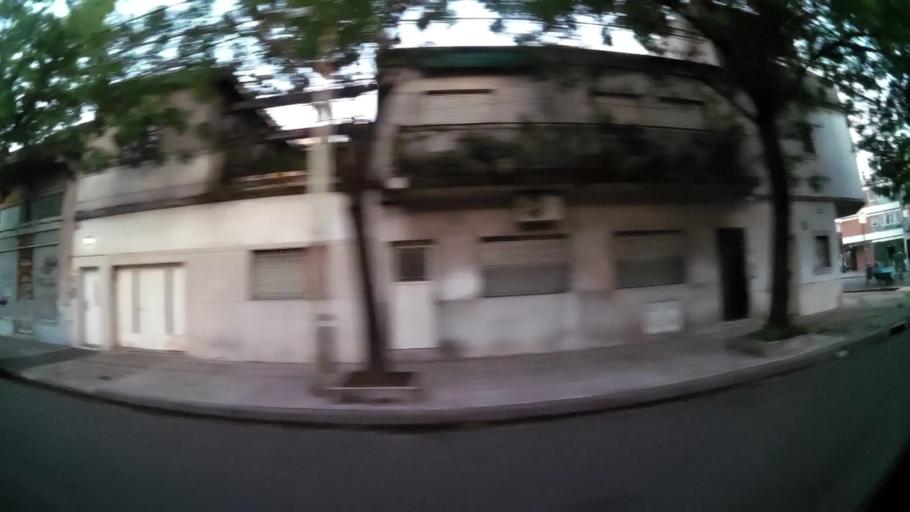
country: AR
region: Buenos Aires F.D.
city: Villa Santa Rita
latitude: -34.6365
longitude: -58.4367
